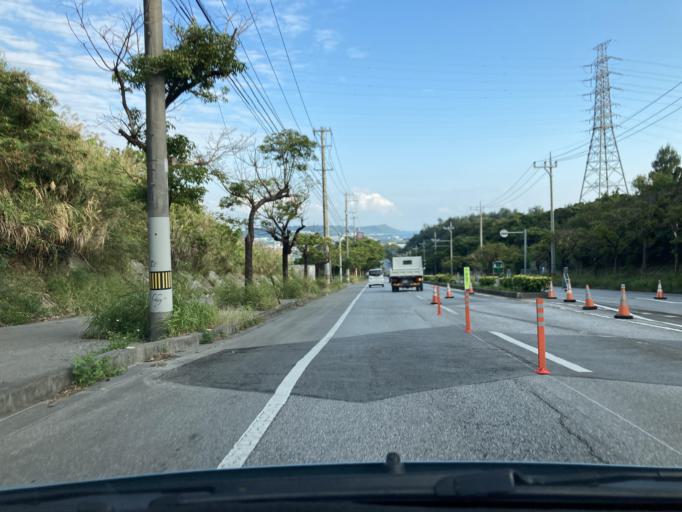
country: JP
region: Okinawa
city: Gushikawa
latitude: 26.3455
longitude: 127.8373
